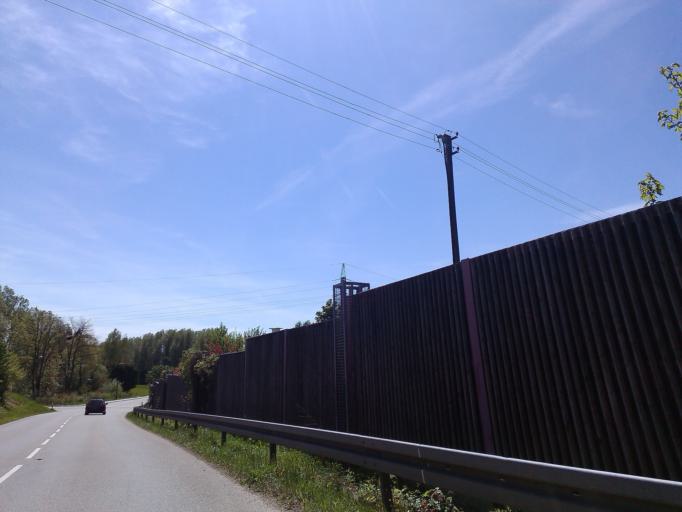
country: DE
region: Bavaria
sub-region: Upper Bavaria
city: Starnberg
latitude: 48.0079
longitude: 11.3486
